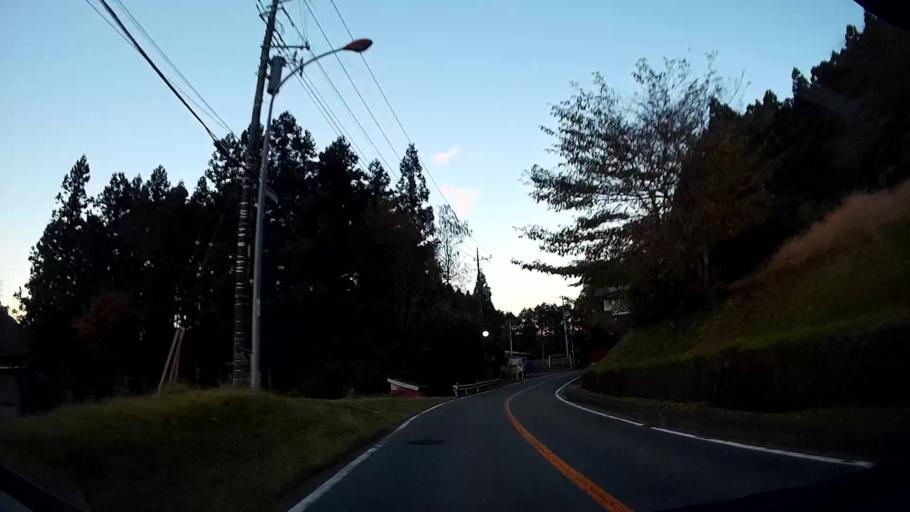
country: JP
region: Yamanashi
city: Uenohara
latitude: 35.5751
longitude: 139.2234
